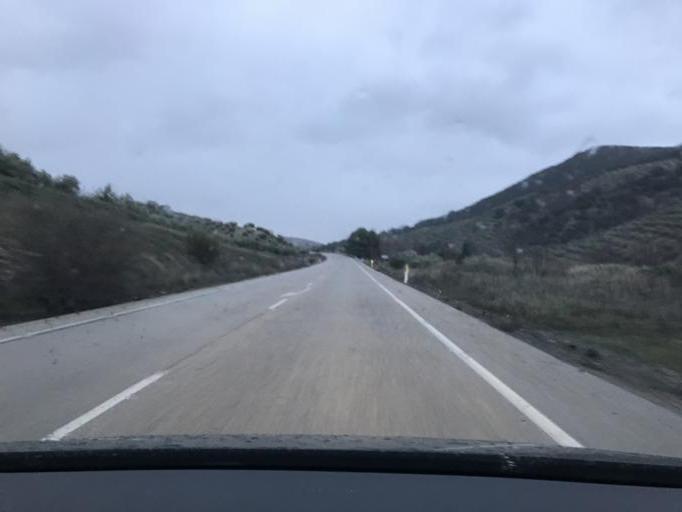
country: ES
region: Andalusia
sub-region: Provincia de Granada
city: Campotejar
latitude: 37.4593
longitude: -3.6080
